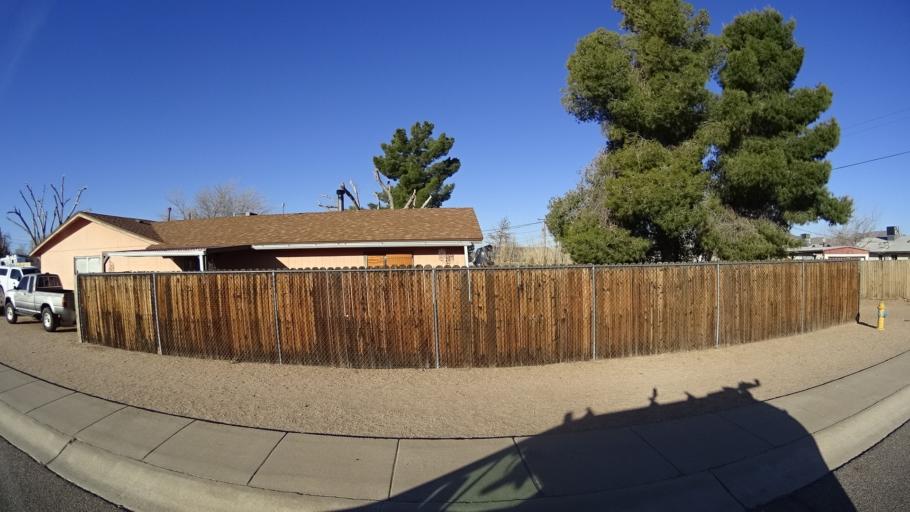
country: US
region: Arizona
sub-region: Mohave County
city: Kingman
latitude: 35.1943
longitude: -114.0155
